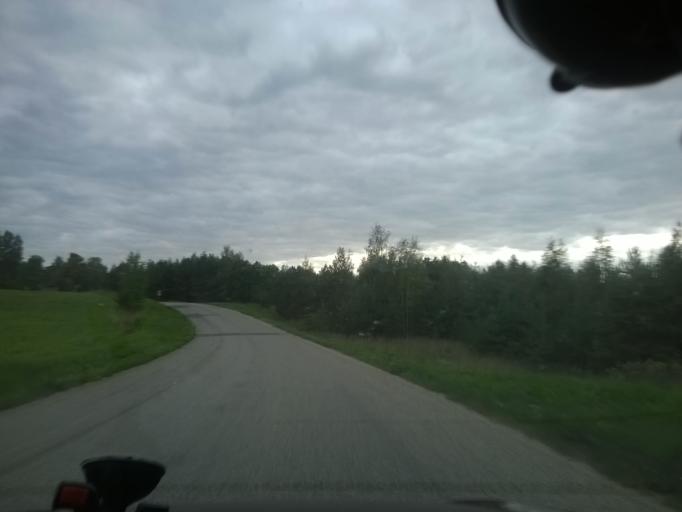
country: EE
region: Vorumaa
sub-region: Voru linn
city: Voru
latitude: 57.8131
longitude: 27.0958
